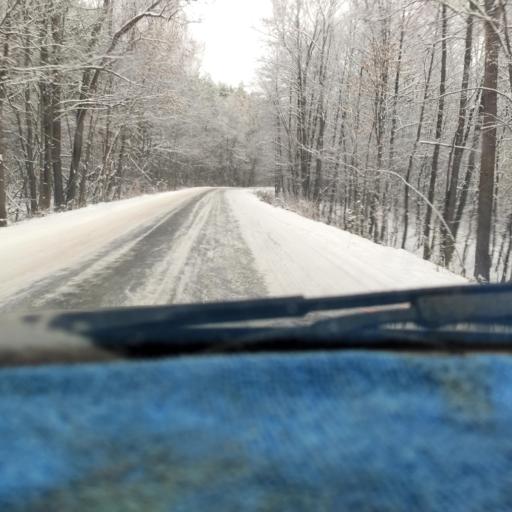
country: RU
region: Bashkortostan
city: Avdon
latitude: 54.6721
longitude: 55.8395
